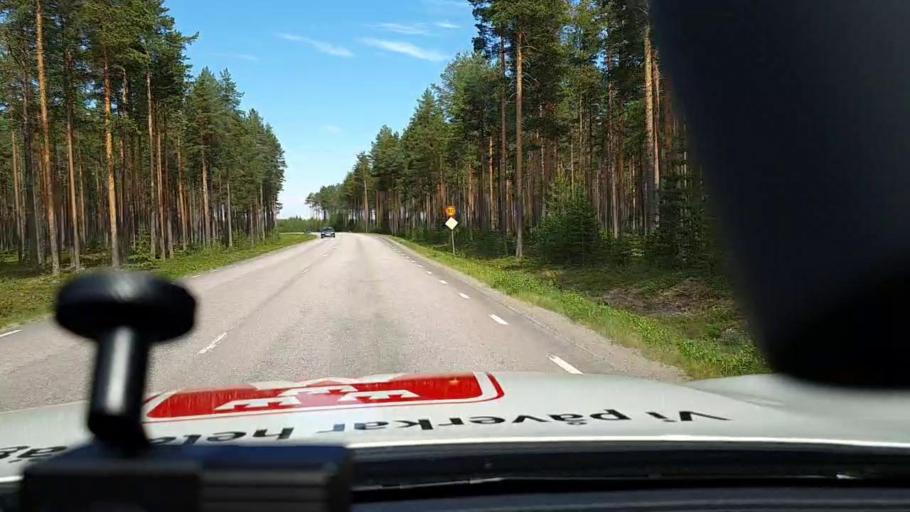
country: SE
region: Norrbotten
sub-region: Lulea Kommun
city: Sodra Sunderbyn
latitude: 65.6309
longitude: 21.9250
